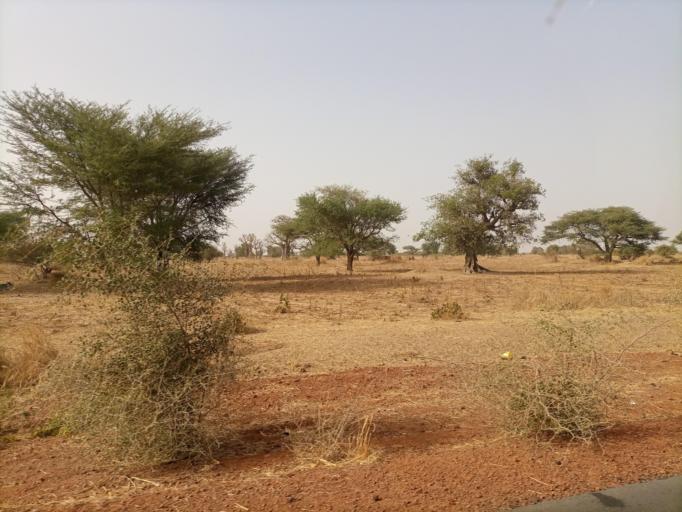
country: SN
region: Fatick
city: Foundiougne
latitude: 14.1255
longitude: -16.4211
